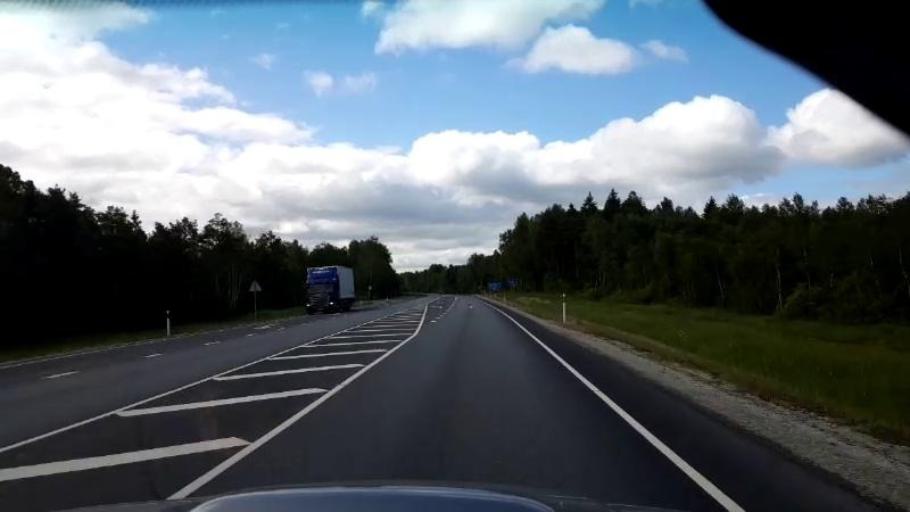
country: EE
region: Raplamaa
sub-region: Maerjamaa vald
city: Marjamaa
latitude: 59.0464
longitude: 24.4435
